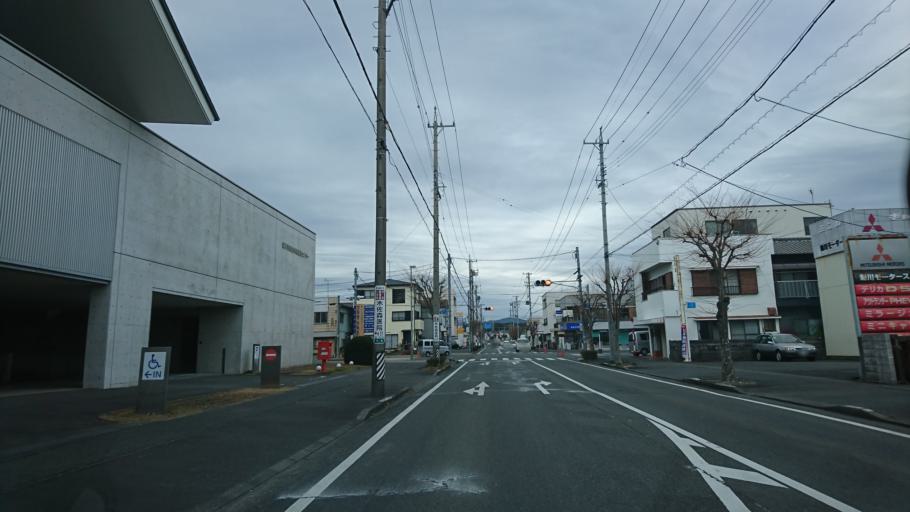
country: JP
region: Shizuoka
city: Kanaya
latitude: 34.7597
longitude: 138.0886
